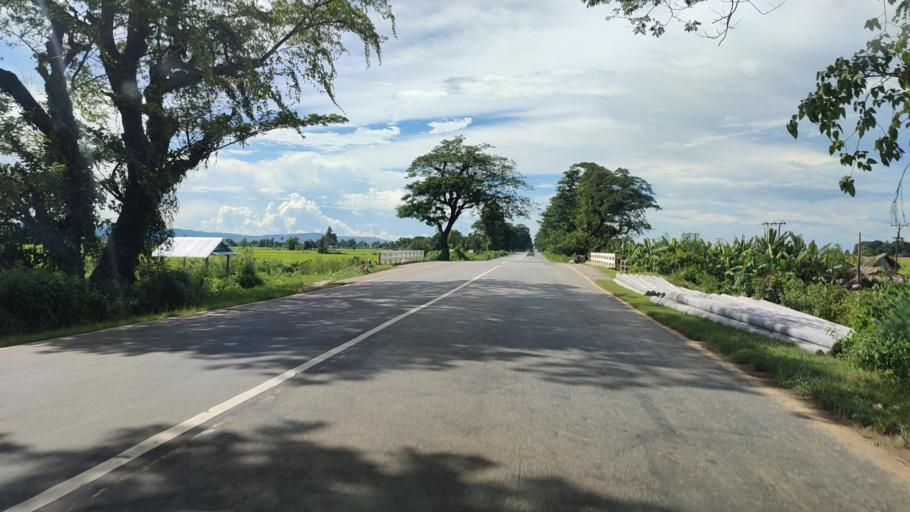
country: MM
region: Bago
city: Pyu
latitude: 18.3005
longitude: 96.5102
